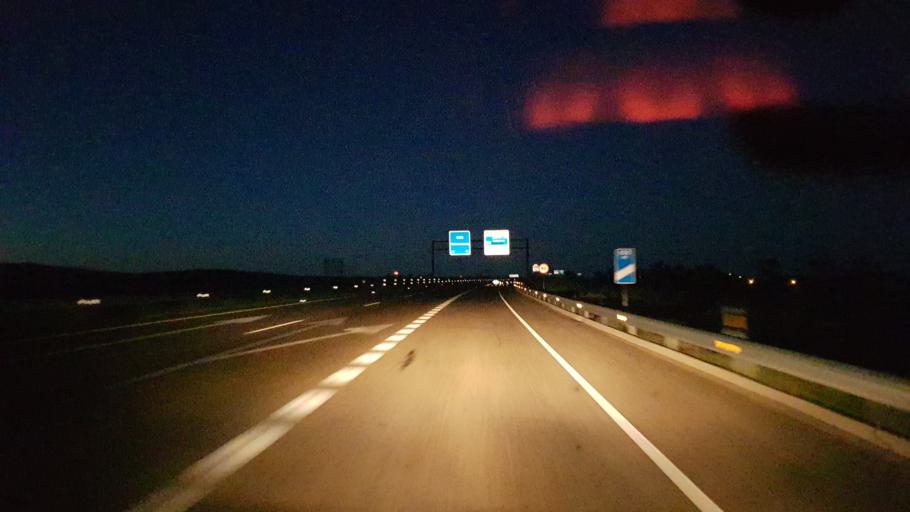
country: ES
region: Castille and Leon
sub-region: Provincia de Zamora
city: Monfarracinos
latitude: 41.5376
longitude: -5.7069
